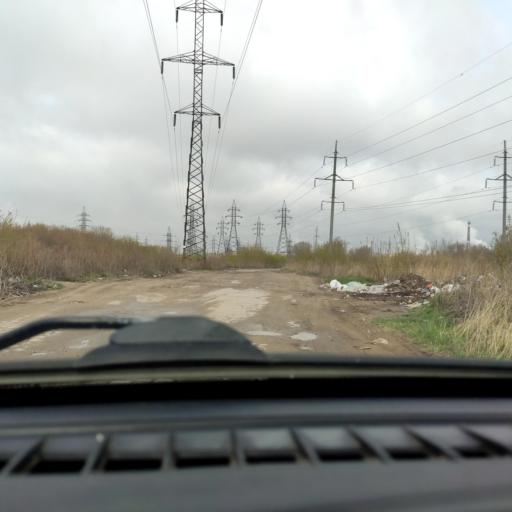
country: RU
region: Samara
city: Zhigulevsk
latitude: 53.5387
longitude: 49.4986
